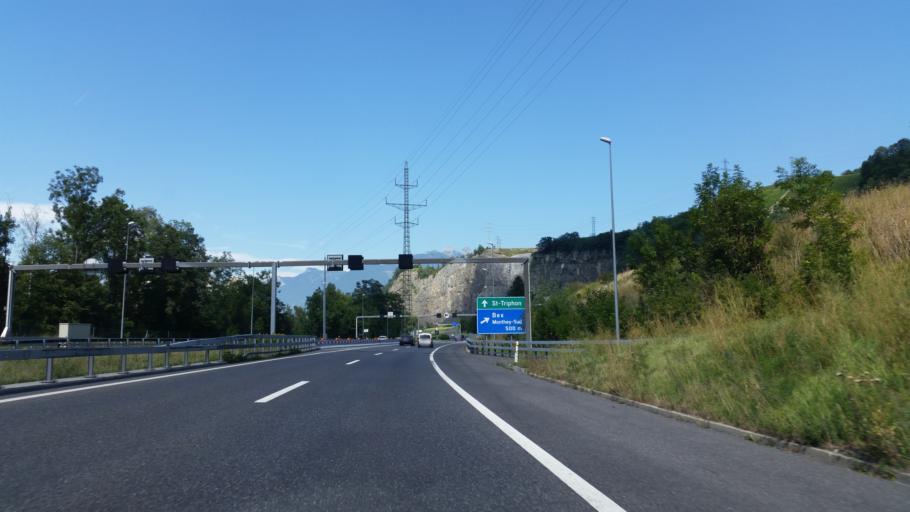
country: CH
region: Valais
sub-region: Saint-Maurice District
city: Saint-Maurice
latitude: 46.2268
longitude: 7.0039
